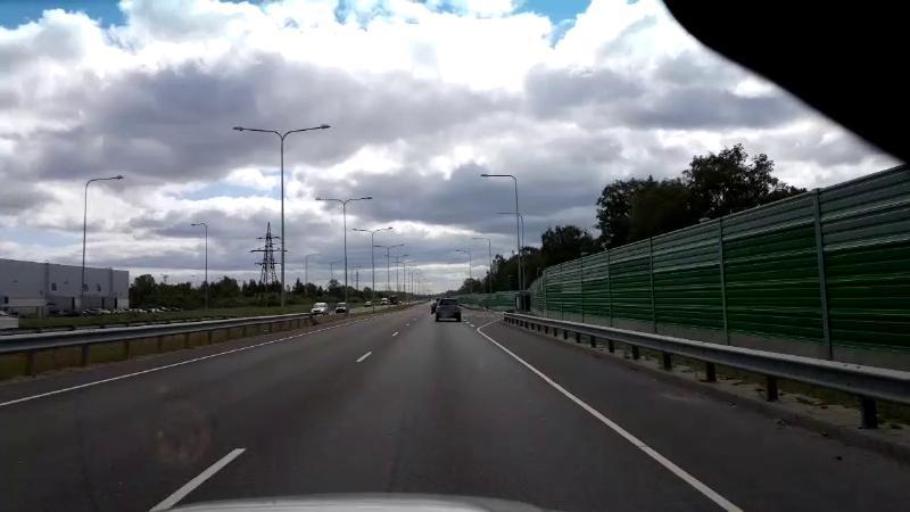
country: EE
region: Paernumaa
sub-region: Paernu linn
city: Parnu
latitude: 58.3956
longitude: 24.5275
